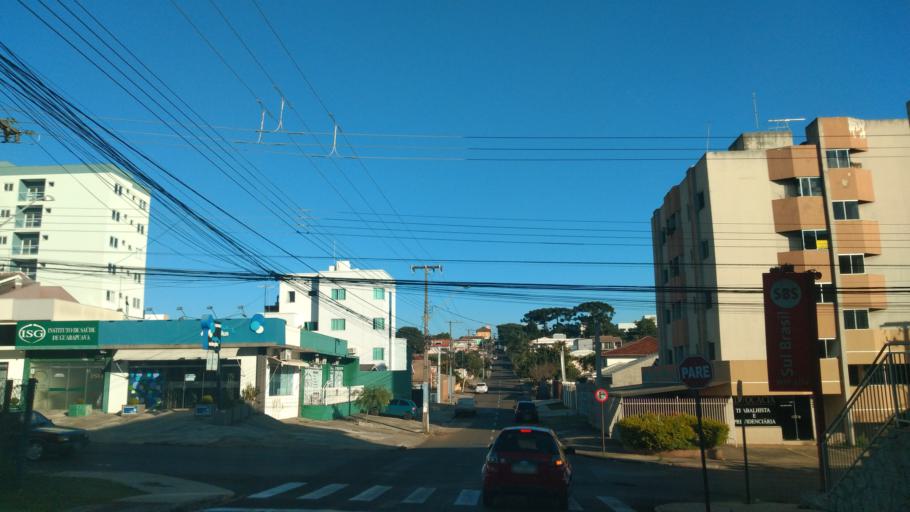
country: BR
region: Parana
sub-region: Guarapuava
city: Guarapuava
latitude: -25.3984
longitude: -51.4645
